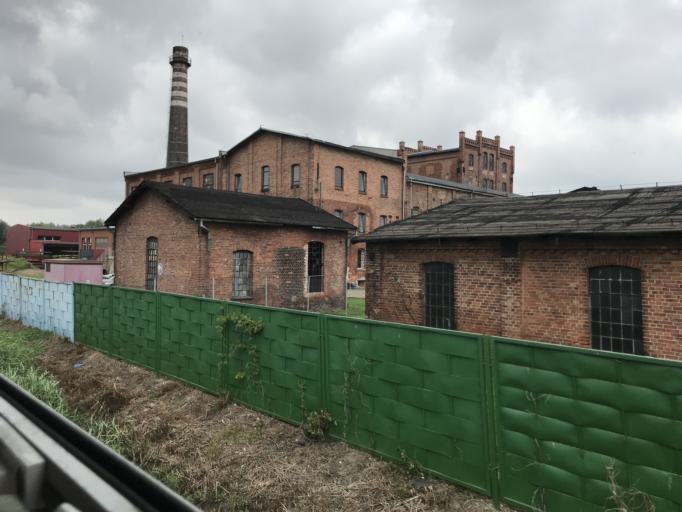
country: PL
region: Pomeranian Voivodeship
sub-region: Powiat malborski
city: Stare Pole
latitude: 54.0521
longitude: 19.1991
